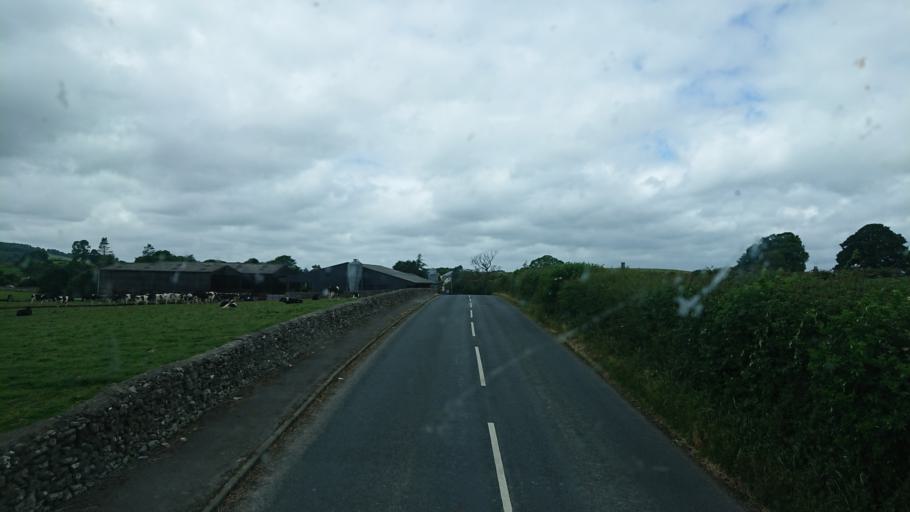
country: GB
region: England
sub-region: Cumbria
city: Milnthorpe
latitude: 54.2292
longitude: -2.7554
